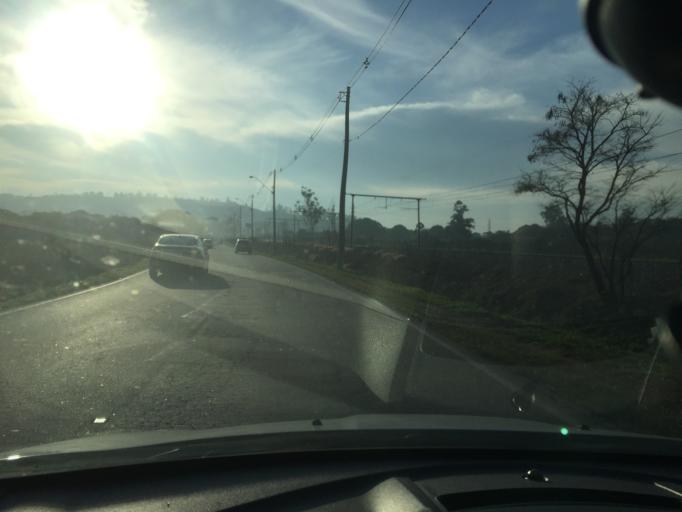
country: BR
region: Sao Paulo
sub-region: Varzea Paulista
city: Varzea Paulista
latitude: -23.2031
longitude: -46.8508
